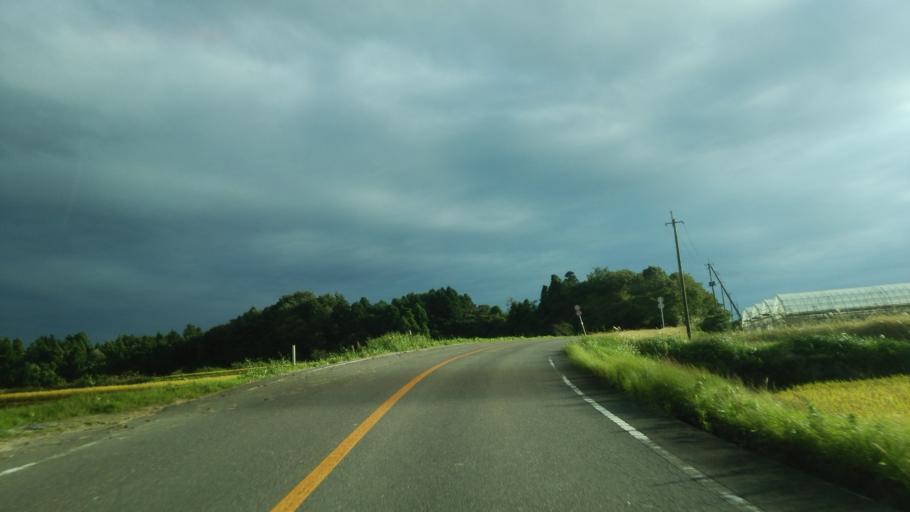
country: JP
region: Fukushima
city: Sukagawa
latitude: 37.3399
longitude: 140.3295
